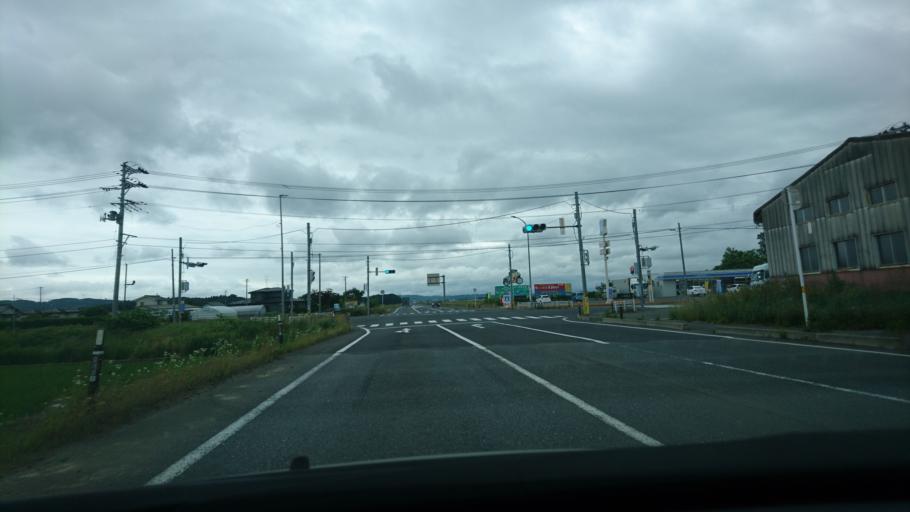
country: JP
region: Miyagi
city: Wakuya
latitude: 38.7086
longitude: 141.2599
